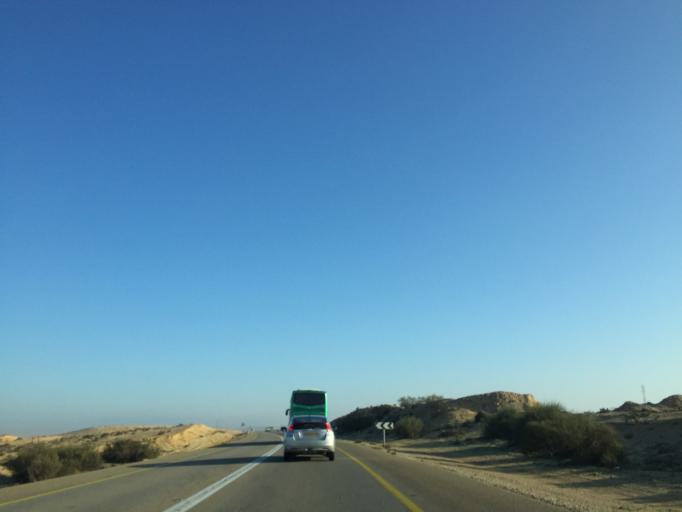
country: IL
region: Southern District
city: Yeroham
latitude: 31.0270
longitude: 34.9696
